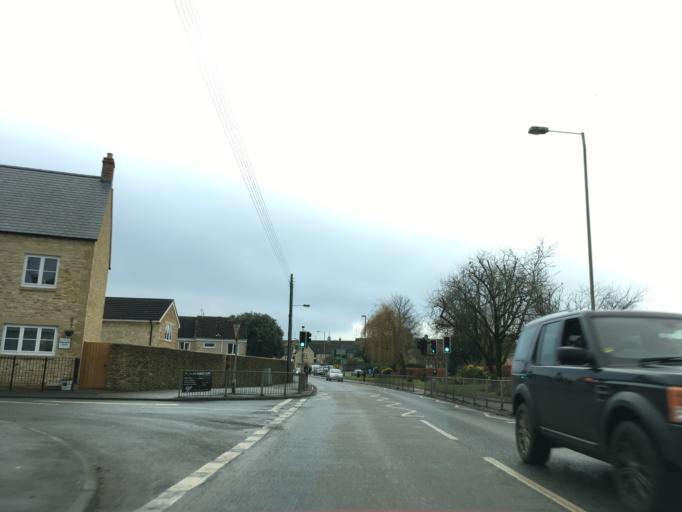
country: GB
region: England
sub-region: Gloucestershire
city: Tetbury
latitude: 51.6410
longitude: -2.1600
